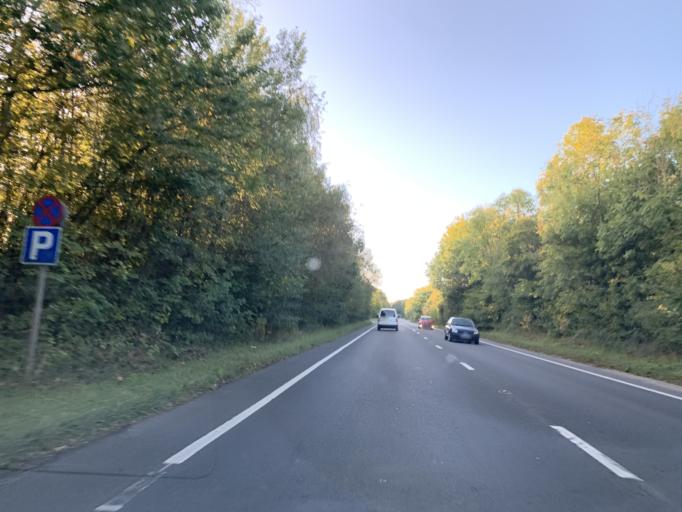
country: GB
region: England
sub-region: Wiltshire
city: Whiteparish
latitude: 51.0008
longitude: -1.6618
